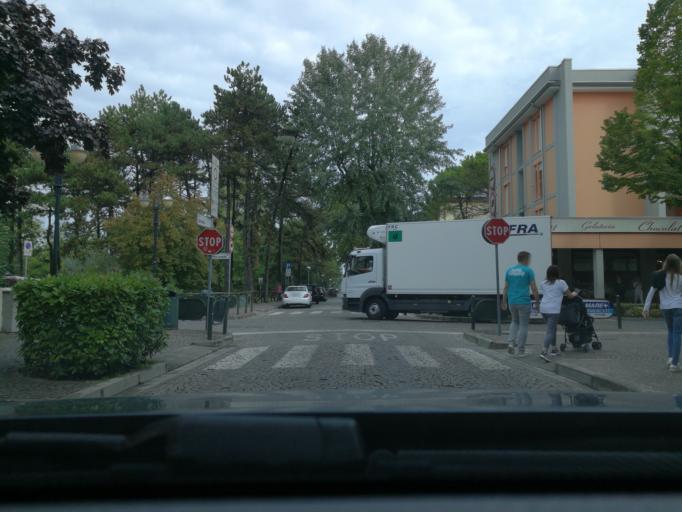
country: IT
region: Veneto
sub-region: Provincia di Venezia
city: Bibione
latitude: 45.6348
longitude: 13.0438
